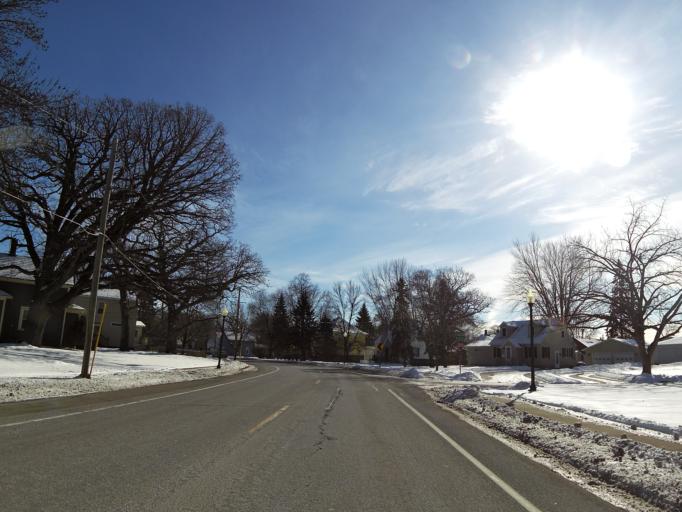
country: US
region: Minnesota
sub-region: Dakota County
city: Hastings
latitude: 44.7446
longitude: -92.8665
